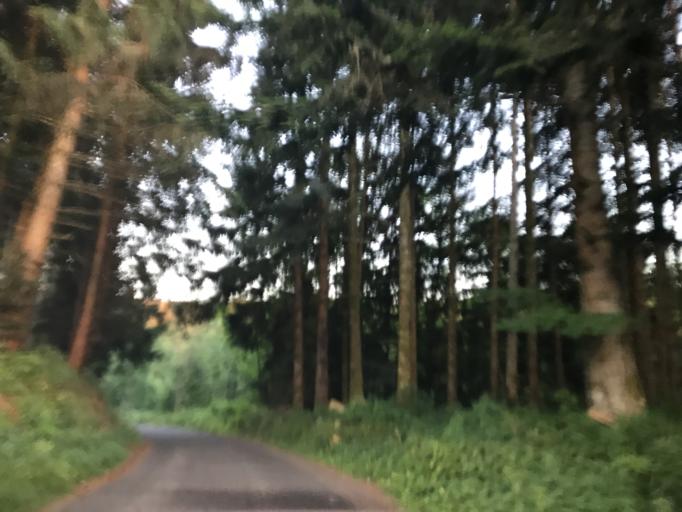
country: FR
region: Rhone-Alpes
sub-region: Departement de la Loire
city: Noiretable
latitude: 45.7669
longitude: 3.7019
